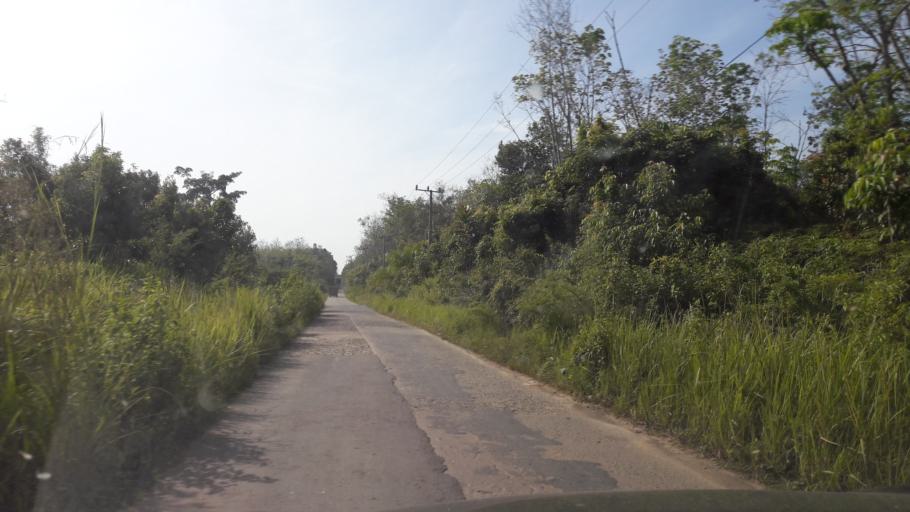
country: ID
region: South Sumatra
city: Gunungmenang
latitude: -3.3133
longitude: 104.0074
